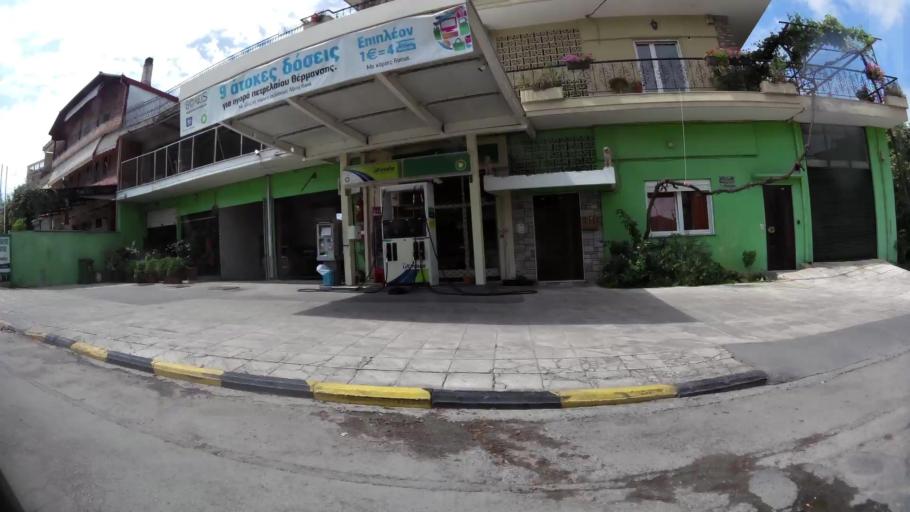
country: GR
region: Central Macedonia
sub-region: Nomos Pierias
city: Katerini
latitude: 40.2726
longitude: 22.4920
